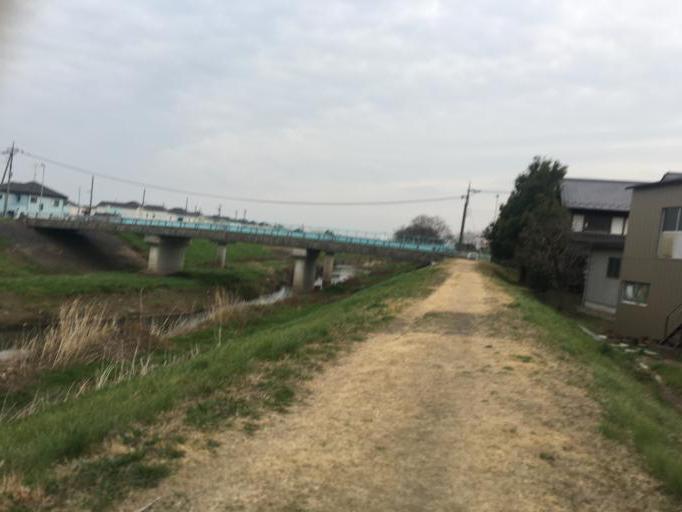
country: JP
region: Saitama
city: Oi
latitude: 35.8682
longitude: 139.5493
